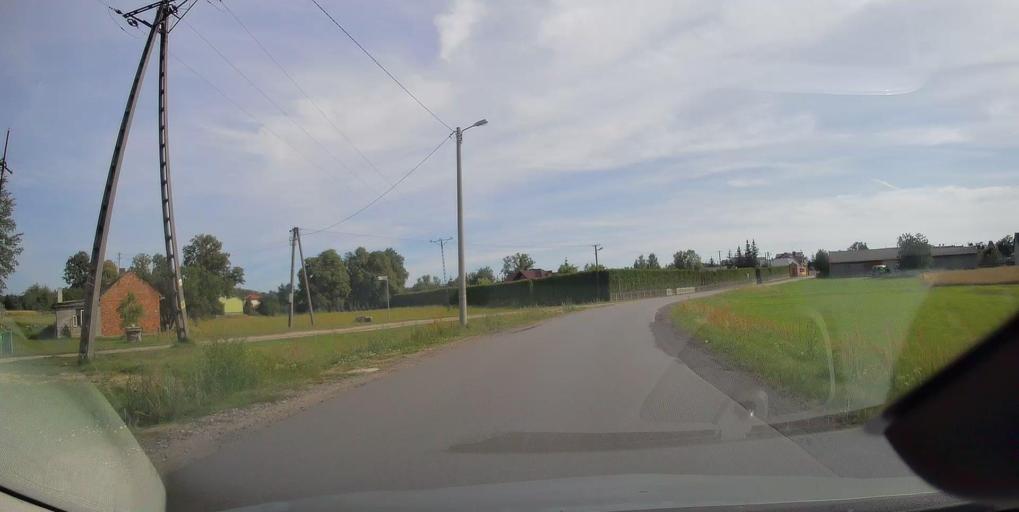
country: PL
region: Lodz Voivodeship
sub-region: Powiat tomaszowski
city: Tomaszow Mazowiecki
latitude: 51.4569
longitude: 20.0359
